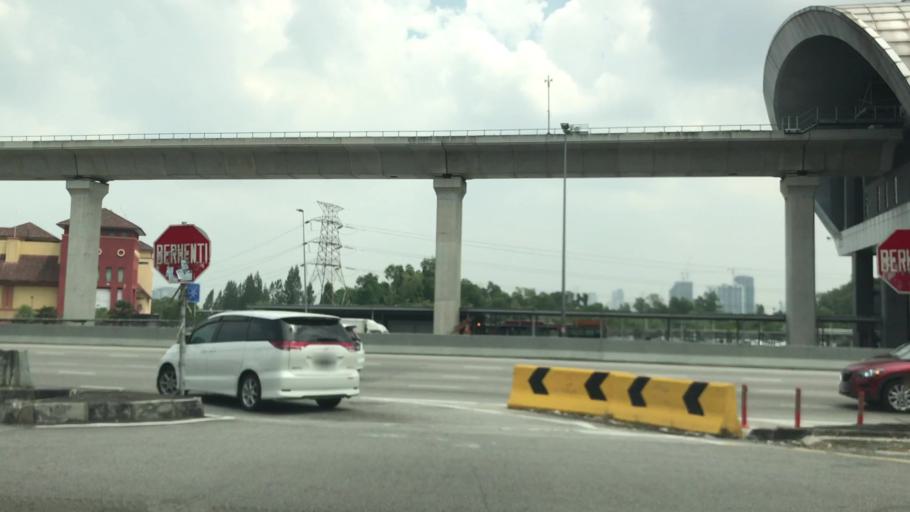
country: MY
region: Selangor
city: Subang Jaya
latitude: 3.0471
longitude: 101.6214
